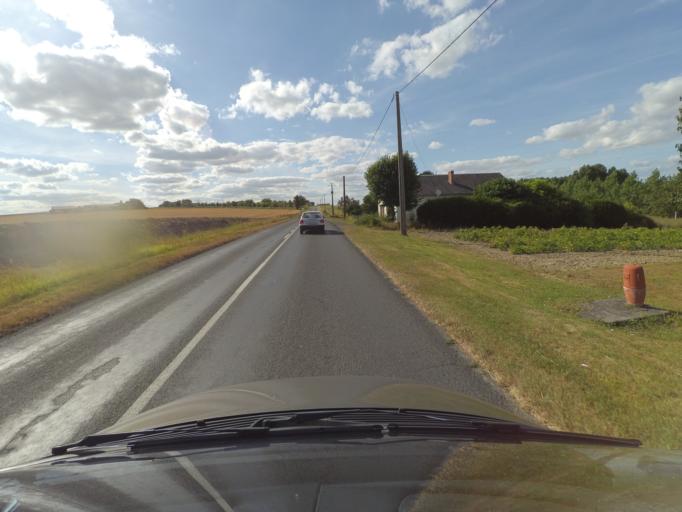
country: FR
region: Poitou-Charentes
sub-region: Departement de la Vienne
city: Saint-Gervais-les-Trois-Clochers
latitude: 46.9516
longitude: 0.4083
